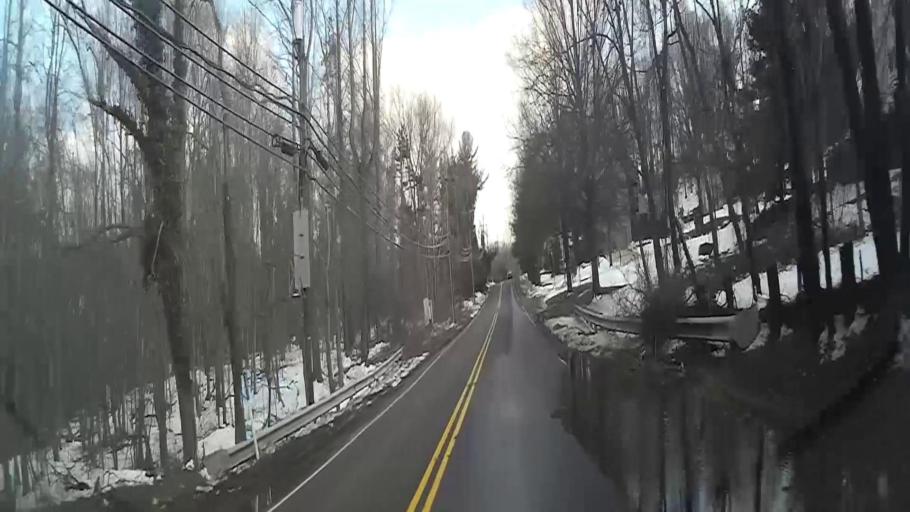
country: US
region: New Jersey
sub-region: Camden County
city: Gibbsboro
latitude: 39.8635
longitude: -74.9546
